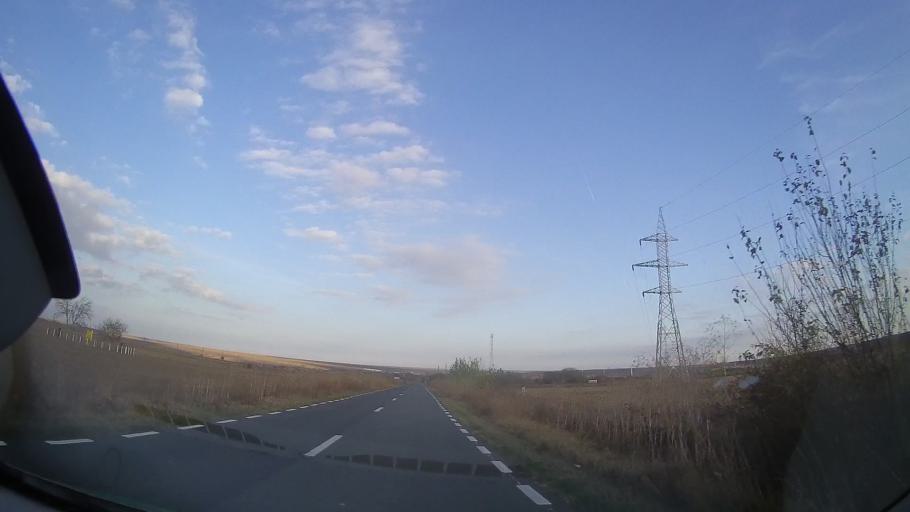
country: RO
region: Constanta
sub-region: Comuna Chirnogeni
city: Plopeni
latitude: 43.9515
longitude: 28.1717
